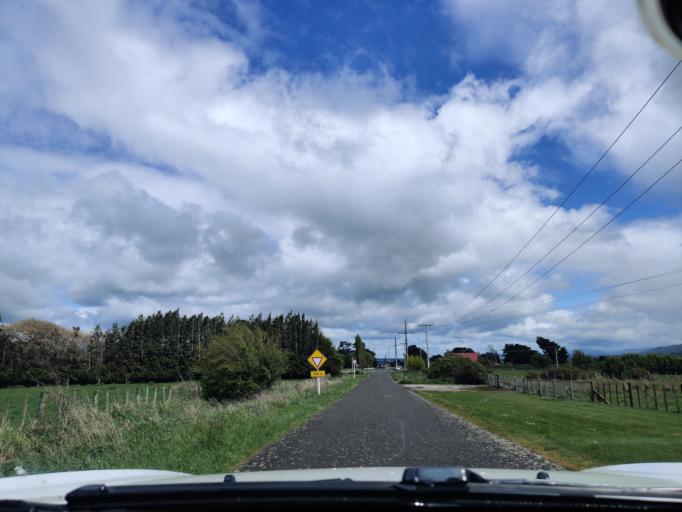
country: NZ
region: Manawatu-Wanganui
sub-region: Palmerston North City
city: Palmerston North
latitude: -40.3160
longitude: 175.8568
